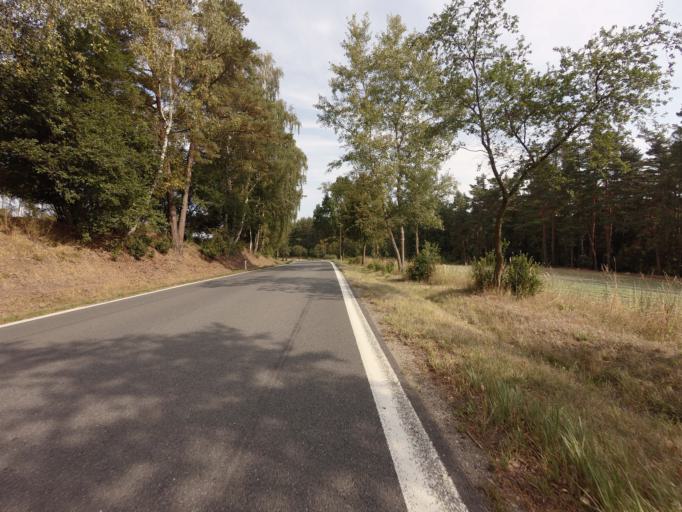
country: CZ
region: Central Bohemia
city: Petrovice
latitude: 49.5290
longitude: 14.3545
